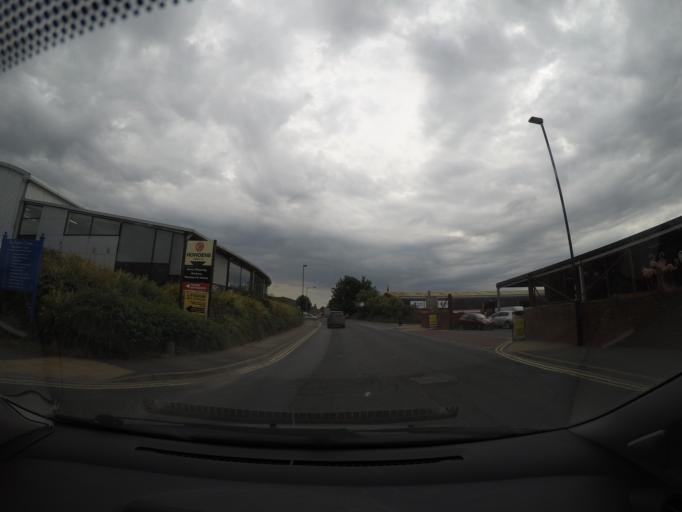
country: GB
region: England
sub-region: City of York
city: York
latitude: 53.9577
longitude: -1.0679
